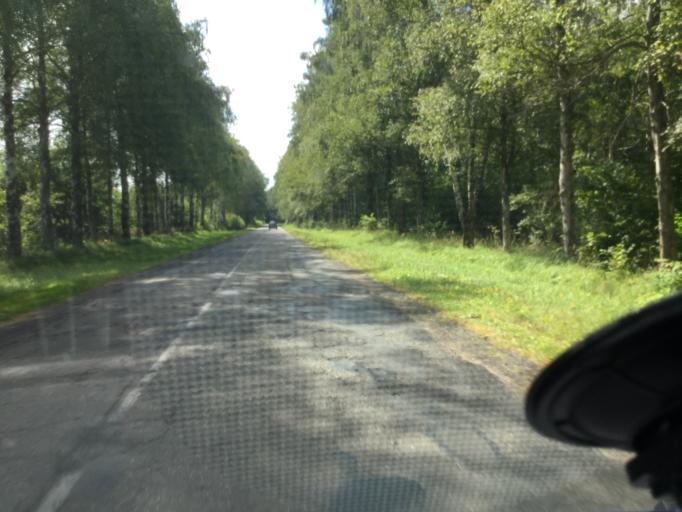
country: BY
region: Vitebsk
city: Chashniki
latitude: 55.3031
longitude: 29.3940
